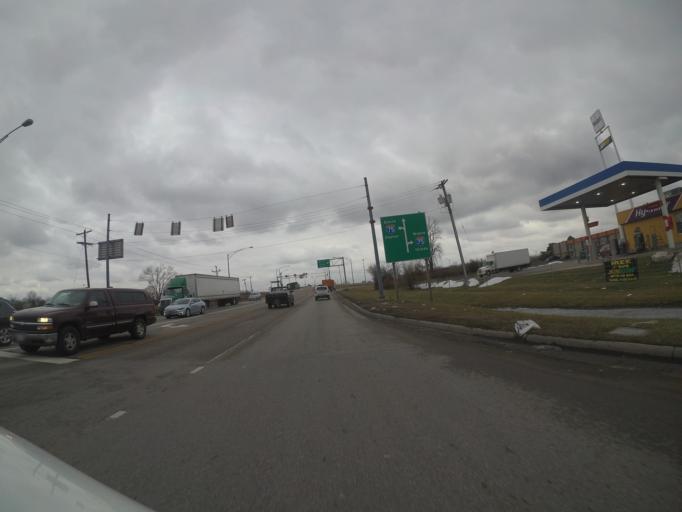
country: US
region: Ohio
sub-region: Wood County
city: Rossford
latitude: 41.6090
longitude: -83.5385
